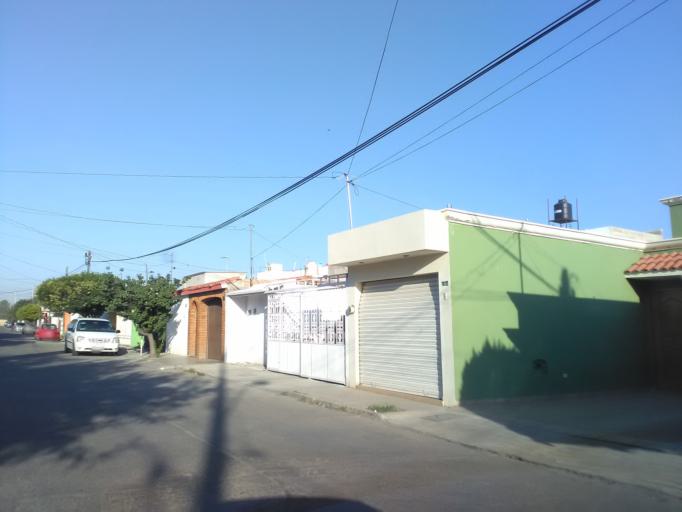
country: MX
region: Durango
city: Victoria de Durango
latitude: 24.0554
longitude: -104.6252
